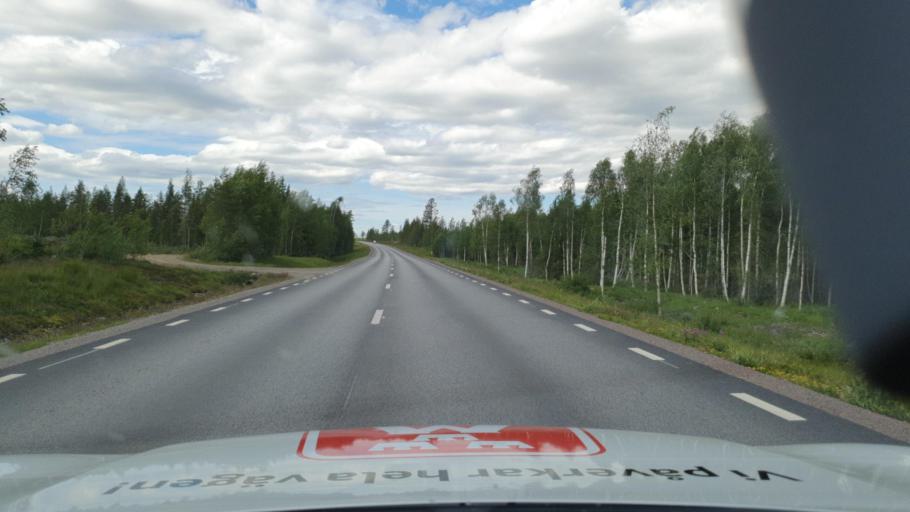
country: SE
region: Vaesterbotten
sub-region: Skelleftea Kommun
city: Langsele
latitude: 65.1118
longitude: 19.9657
